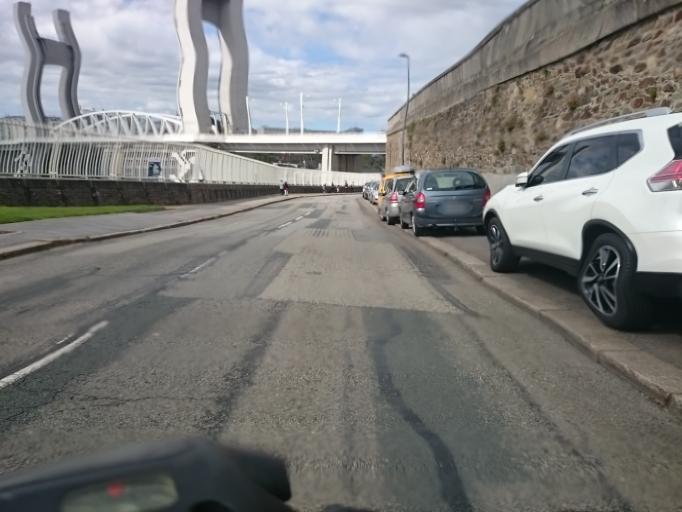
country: FR
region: Brittany
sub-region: Departement du Finistere
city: Brest
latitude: 48.3837
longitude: -4.4938
